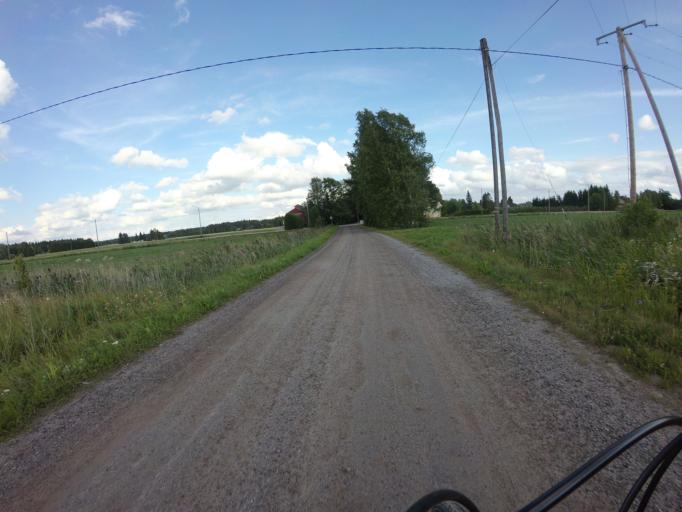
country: FI
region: Varsinais-Suomi
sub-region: Turku
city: Vahto
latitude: 60.5683
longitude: 22.3530
